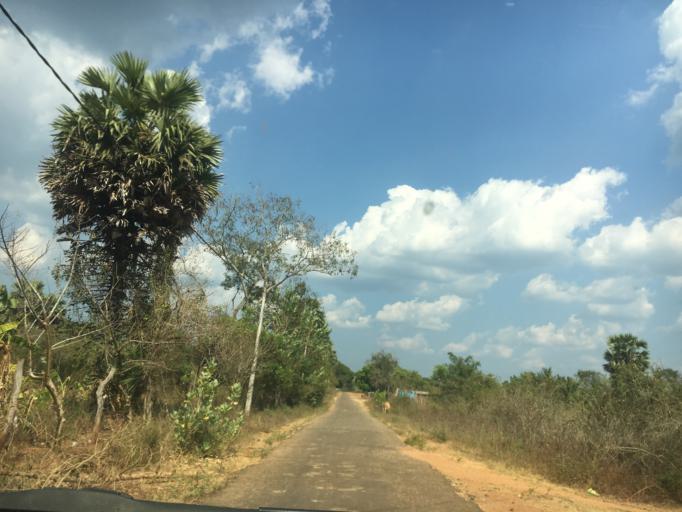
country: LK
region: Northern Province
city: Kilinochchi
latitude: 9.1402
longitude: 80.4453
